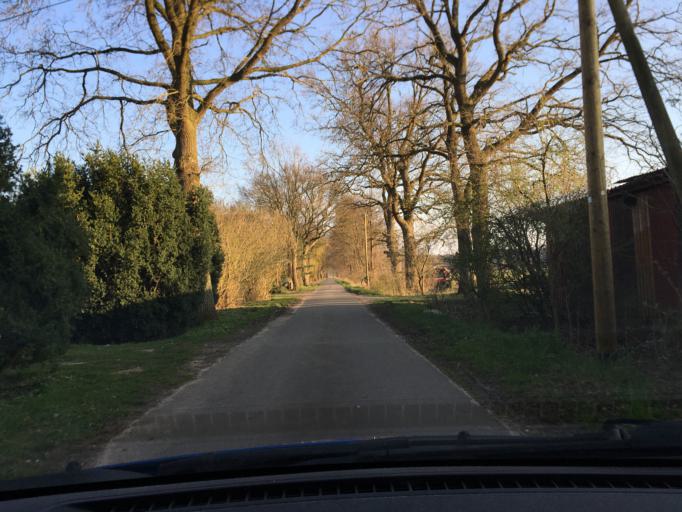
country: DE
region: Lower Saxony
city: Hittbergen
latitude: 53.3266
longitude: 10.6253
